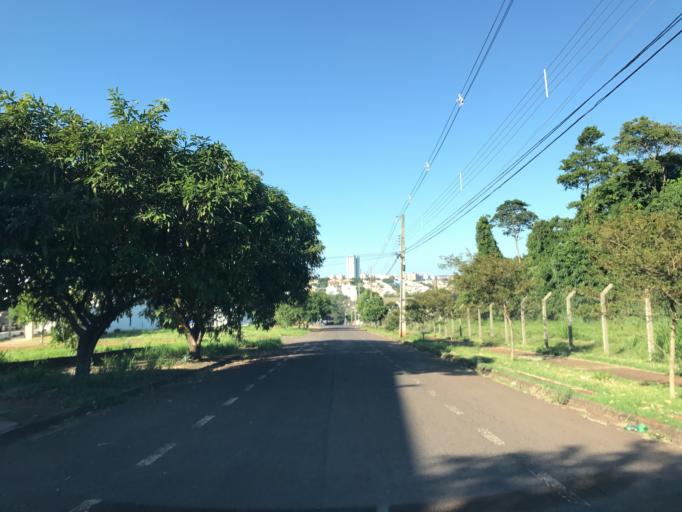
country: BR
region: Parana
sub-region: Maringa
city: Maringa
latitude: -23.4446
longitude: -51.9462
